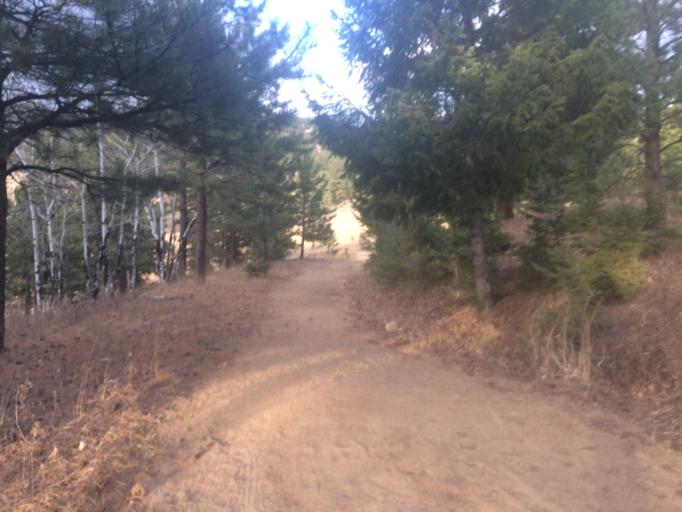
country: US
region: Colorado
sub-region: Boulder County
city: Coal Creek
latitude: 39.9614
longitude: -105.3448
